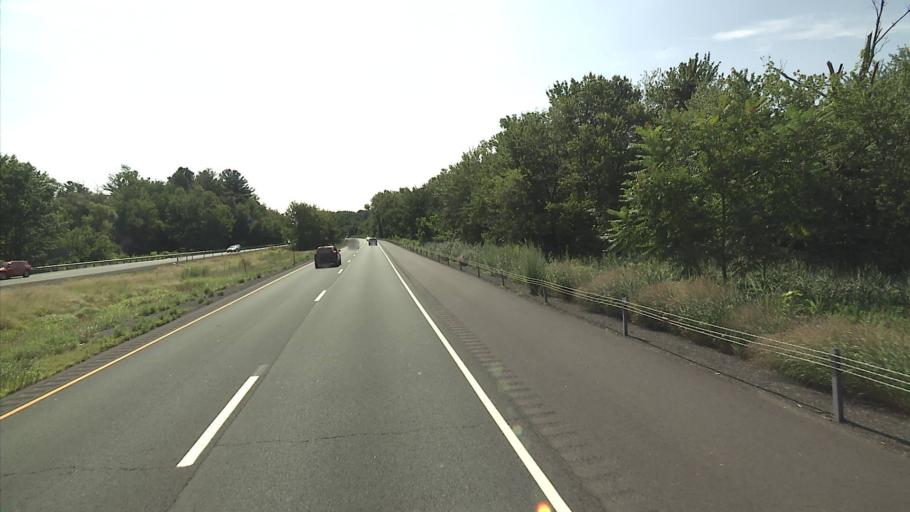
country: US
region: Connecticut
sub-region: Hartford County
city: Glastonbury Center
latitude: 41.7096
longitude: -72.5842
